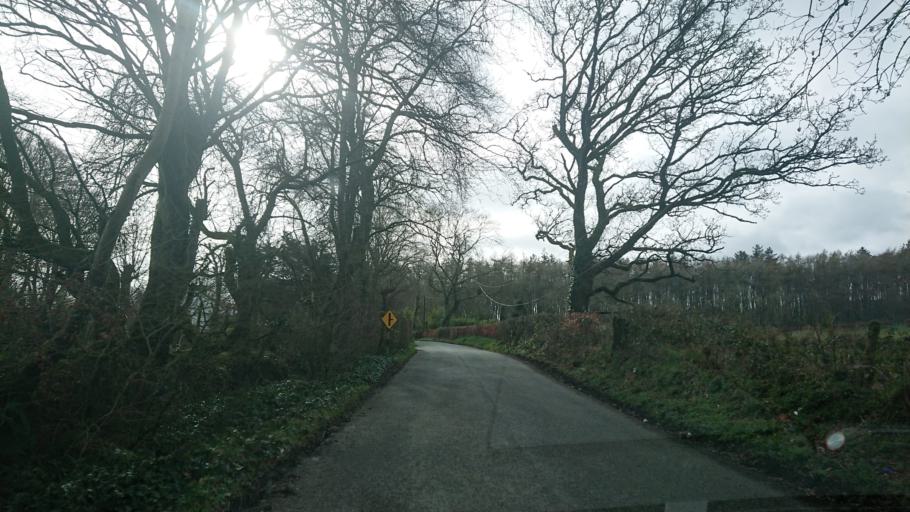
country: IE
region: Leinster
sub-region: Wicklow
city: Blessington
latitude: 53.1553
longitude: -6.5659
